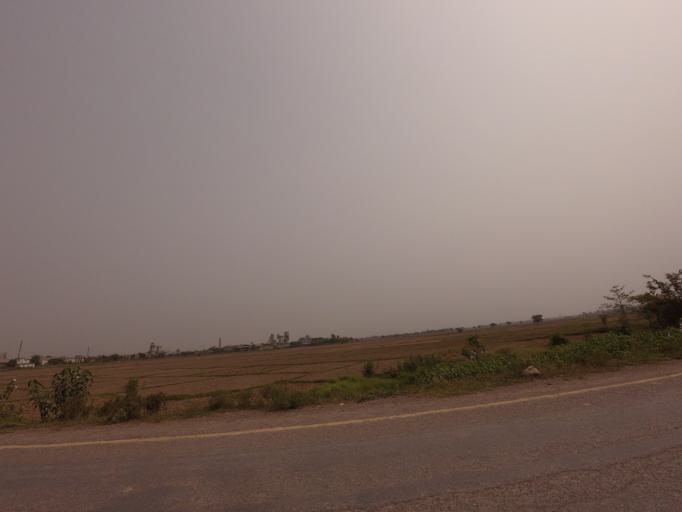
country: NP
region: Western Region
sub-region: Lumbini Zone
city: Bhairahawa
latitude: 27.5040
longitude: 83.3795
